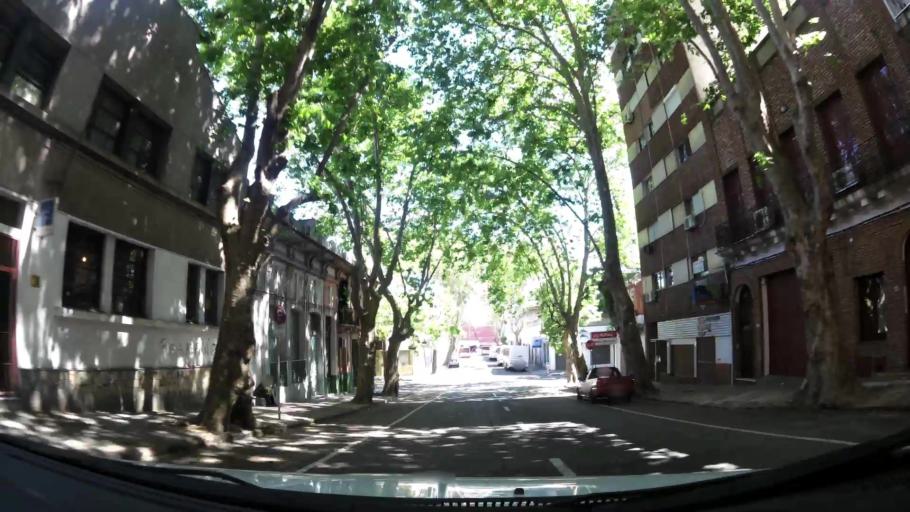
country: UY
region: Montevideo
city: Montevideo
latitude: -34.9020
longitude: -56.1986
